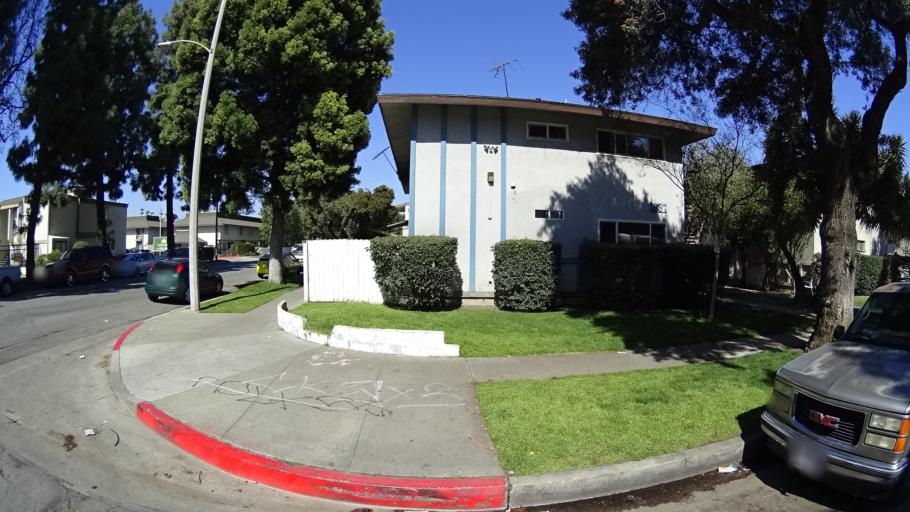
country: US
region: California
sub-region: Orange County
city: Anaheim
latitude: 33.8404
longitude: -117.9472
